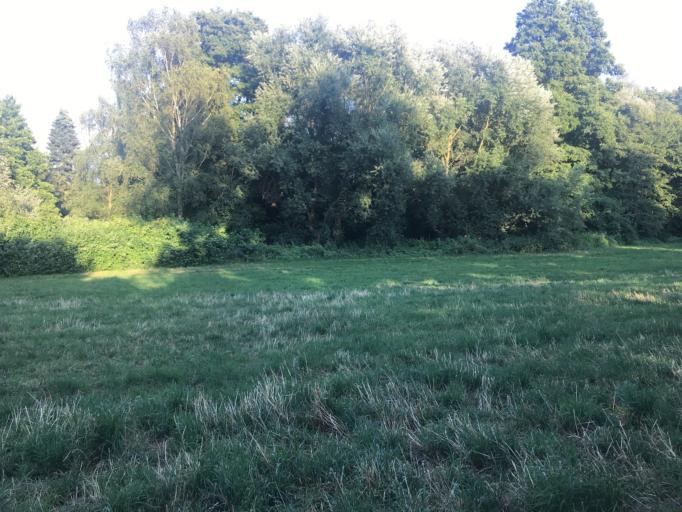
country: DE
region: North Rhine-Westphalia
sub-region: Regierungsbezirk Dusseldorf
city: Krefeld
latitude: 51.3535
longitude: 6.5988
